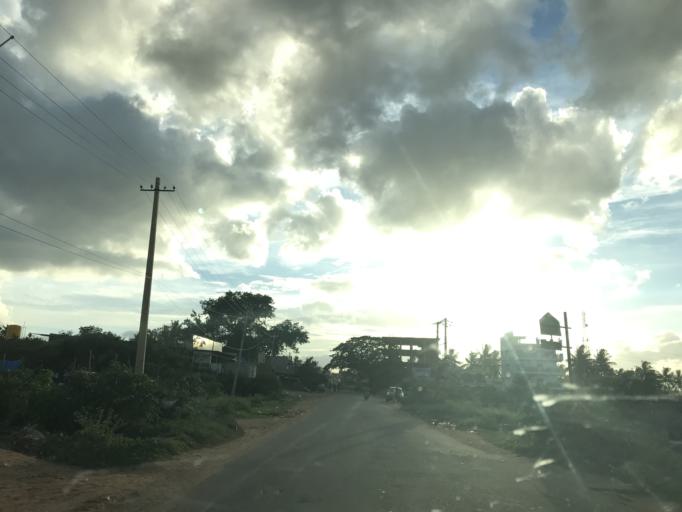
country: IN
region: Karnataka
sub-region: Bangalore Urban
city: Yelahanka
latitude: 13.1337
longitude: 77.6720
